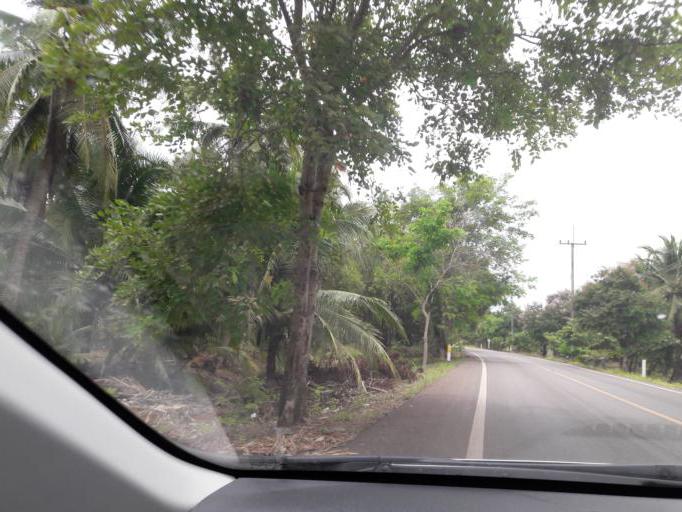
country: TH
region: Samut Sakhon
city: Ban Phaeo
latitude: 13.6162
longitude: 100.0228
